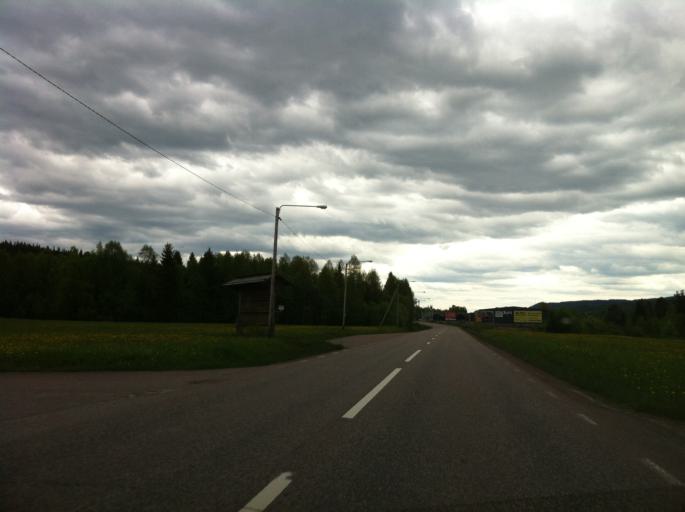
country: SE
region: Dalarna
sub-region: Malung-Saelens kommun
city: Malung
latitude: 61.1395
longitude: 13.2790
